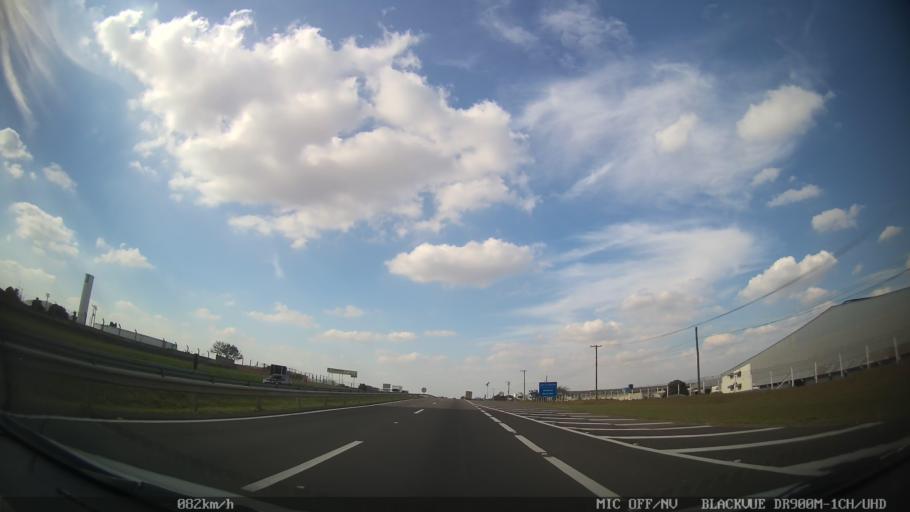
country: BR
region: Sao Paulo
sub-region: Hortolandia
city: Hortolandia
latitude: -22.9086
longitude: -47.2412
